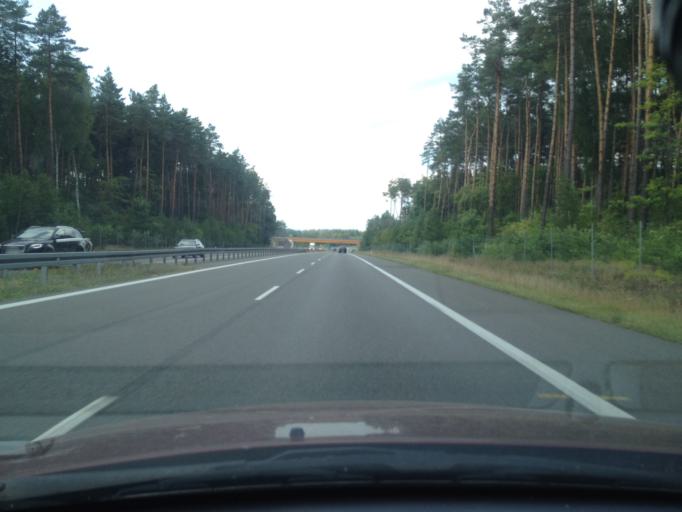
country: PL
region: West Pomeranian Voivodeship
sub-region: Powiat goleniowski
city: Goleniow
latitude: 53.6080
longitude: 14.8212
